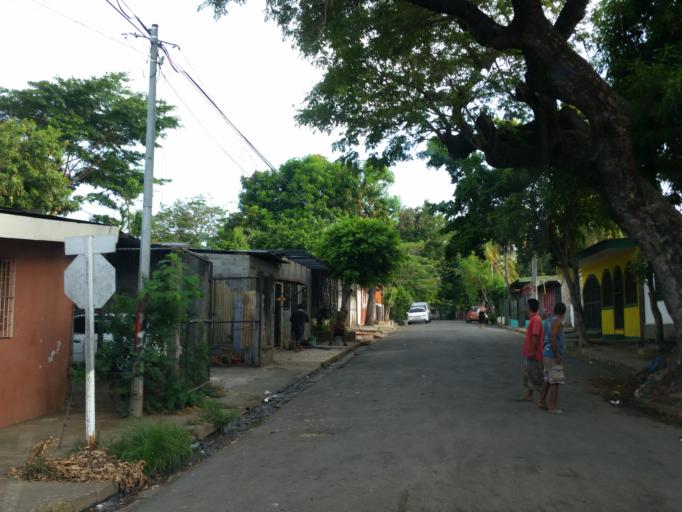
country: NI
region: Managua
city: Managua
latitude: 12.1487
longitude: -86.2781
